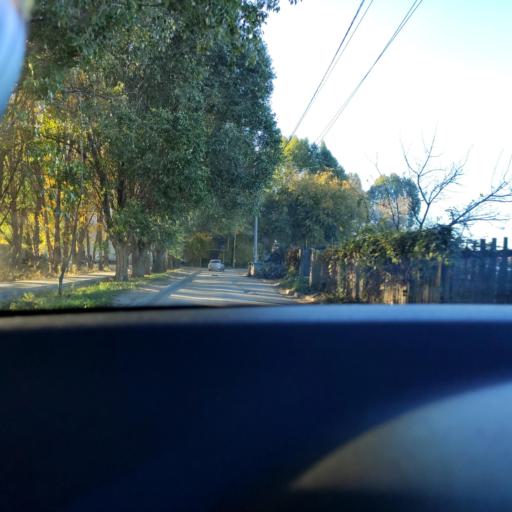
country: RU
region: Samara
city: Smyshlyayevka
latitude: 53.1894
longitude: 50.2828
